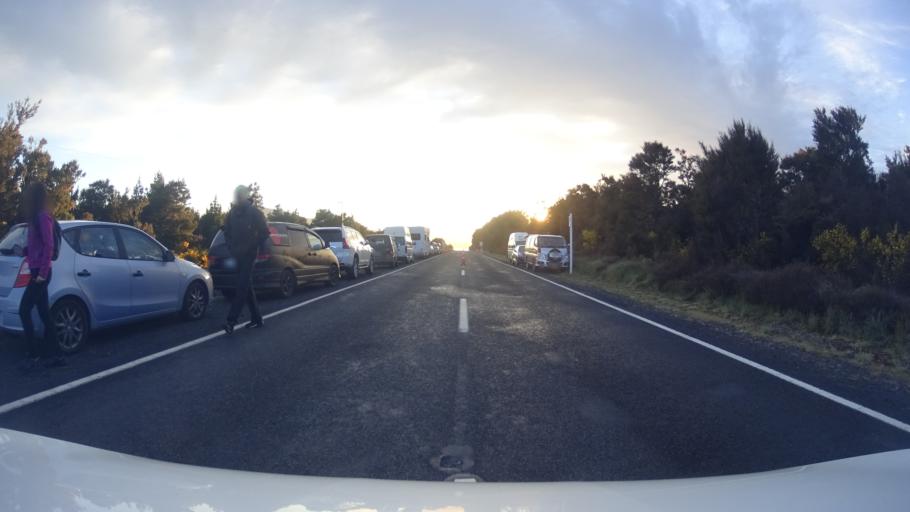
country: NZ
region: Waikato
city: Turangi
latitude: -39.0657
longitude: 175.6680
